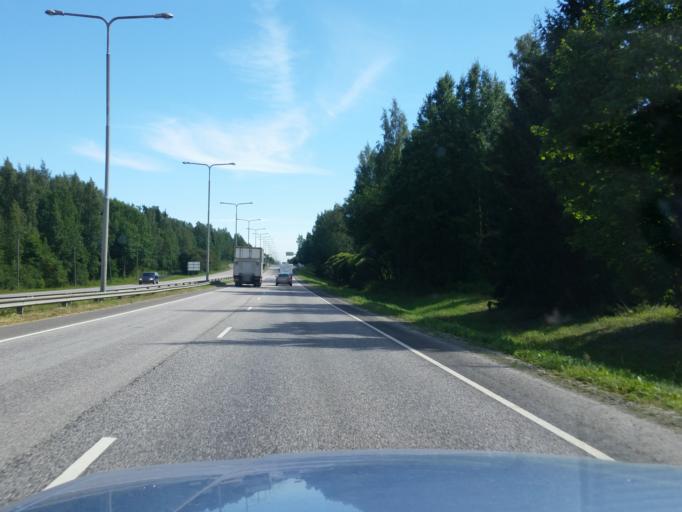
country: FI
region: Uusimaa
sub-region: Helsinki
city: Teekkarikylae
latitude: 60.2504
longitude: 24.8856
